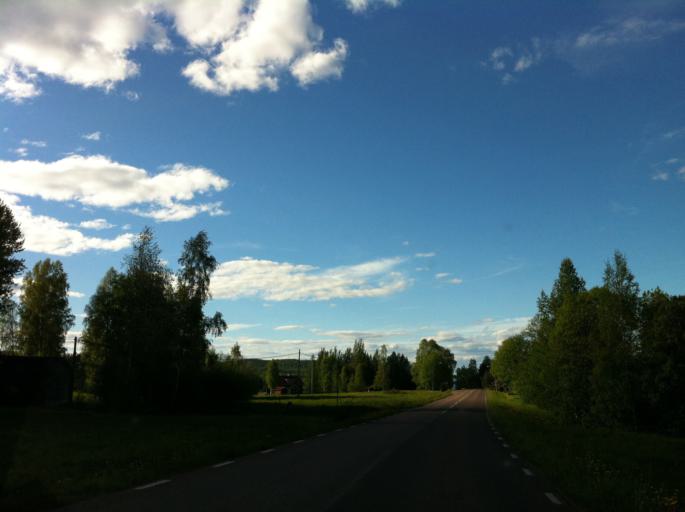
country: SE
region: Dalarna
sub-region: Leksand Municipality
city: Leksand
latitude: 60.7551
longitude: 14.9428
